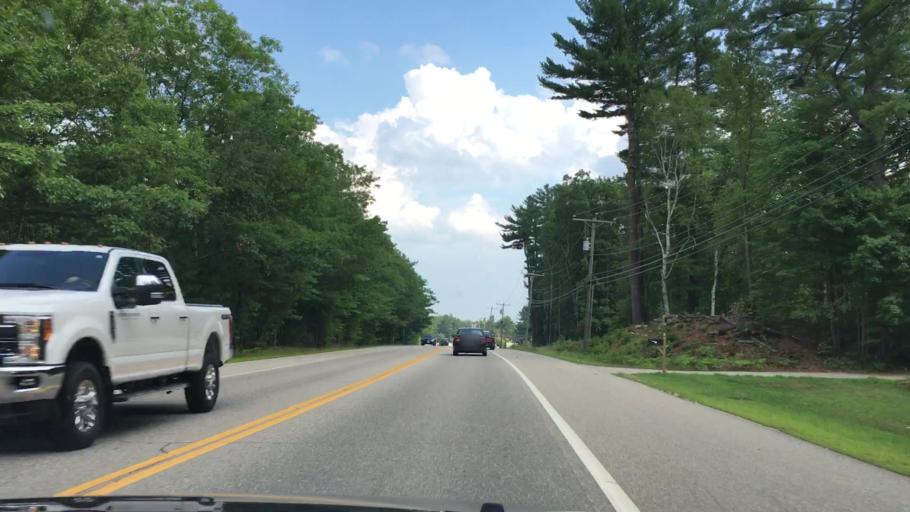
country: US
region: New Hampshire
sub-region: Strafford County
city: Farmington
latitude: 43.3465
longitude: -71.0233
